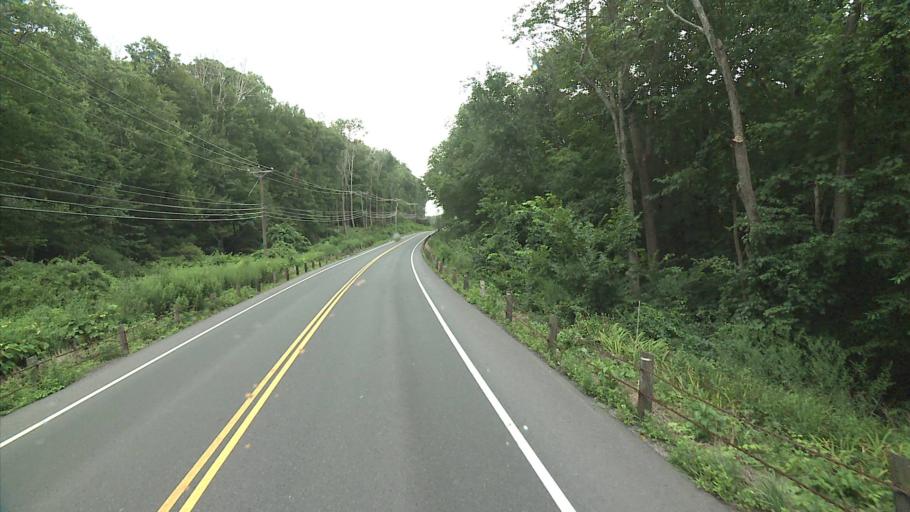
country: US
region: Connecticut
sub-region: New Haven County
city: Southbury
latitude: 41.4708
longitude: -73.1804
